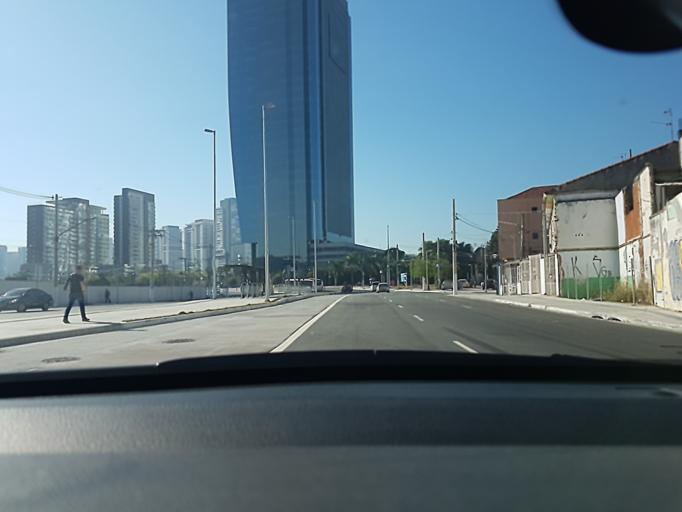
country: BR
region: Sao Paulo
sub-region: Taboao Da Serra
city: Taboao da Serra
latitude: -23.6268
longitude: -46.7049
